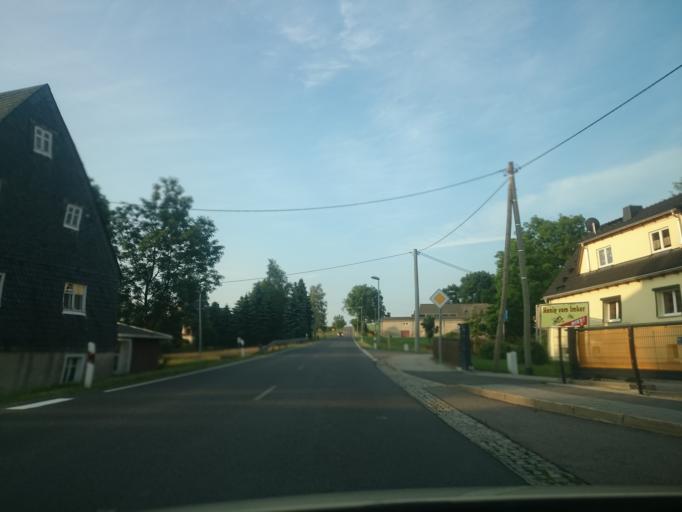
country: DE
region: Saxony
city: Grosshartmannsdorf
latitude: 50.7855
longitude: 13.3206
